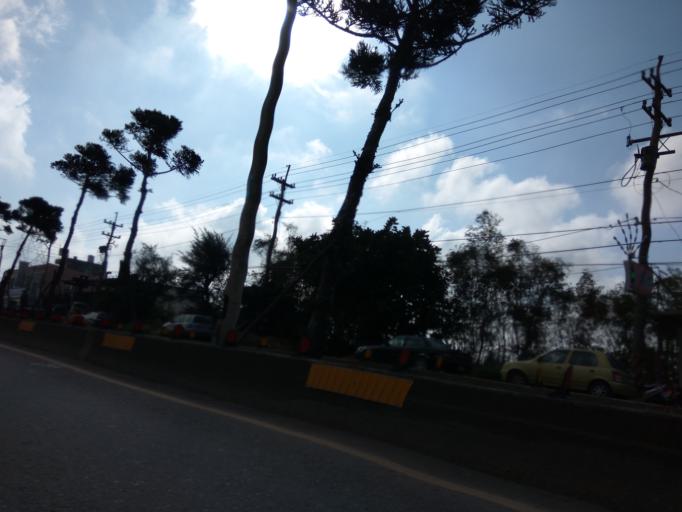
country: TW
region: Taiwan
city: Taoyuan City
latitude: 25.0377
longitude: 121.1031
